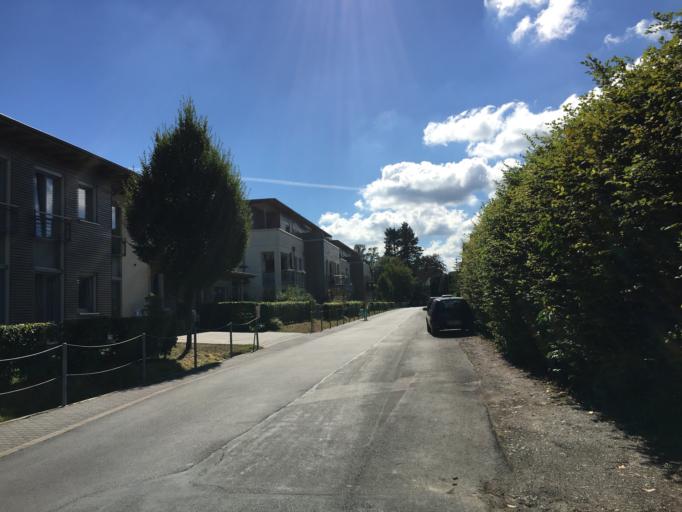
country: DE
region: North Rhine-Westphalia
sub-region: Regierungsbezirk Detmold
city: Detmold
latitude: 51.9264
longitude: 8.8479
